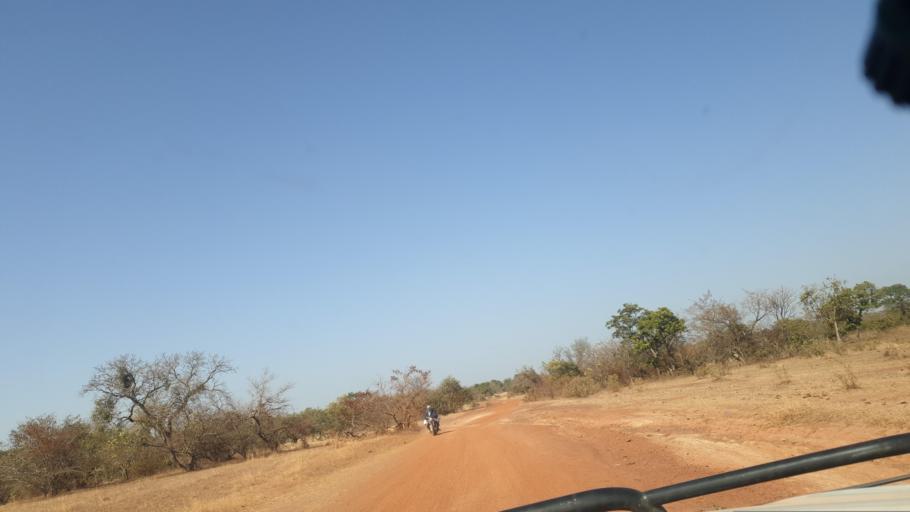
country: ML
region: Sikasso
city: Bougouni
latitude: 11.8187
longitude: -6.9451
